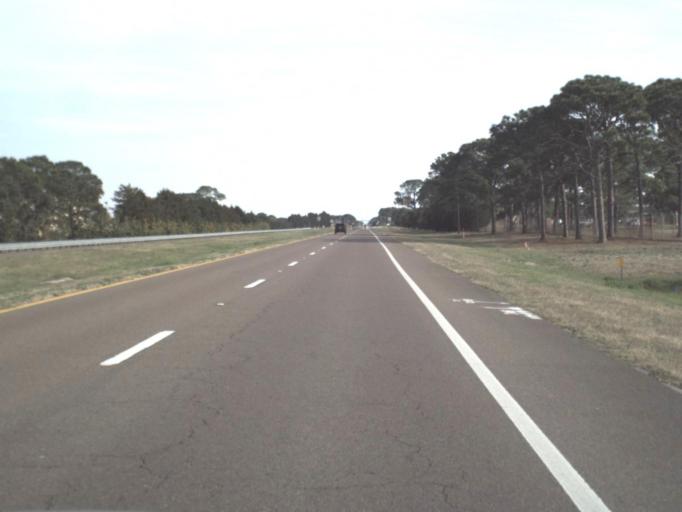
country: US
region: Florida
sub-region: Bay County
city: Tyndall Air Force Base
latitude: 30.0760
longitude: -85.5981
